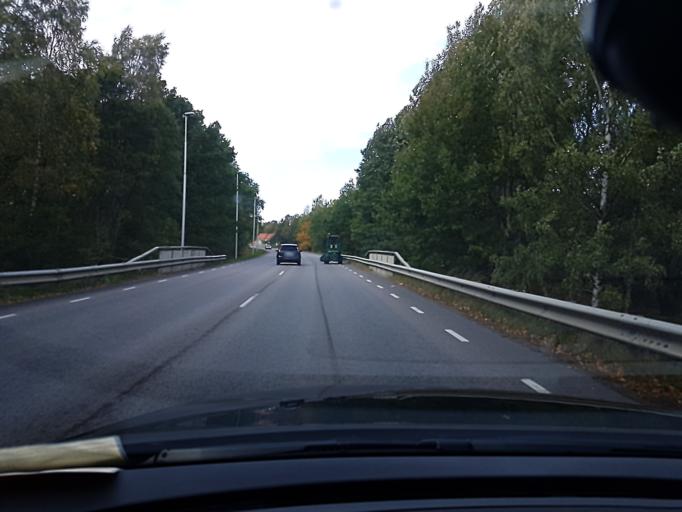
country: SE
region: Kronoberg
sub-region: Vaxjo Kommun
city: Vaexjoe
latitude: 56.8624
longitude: 14.8057
